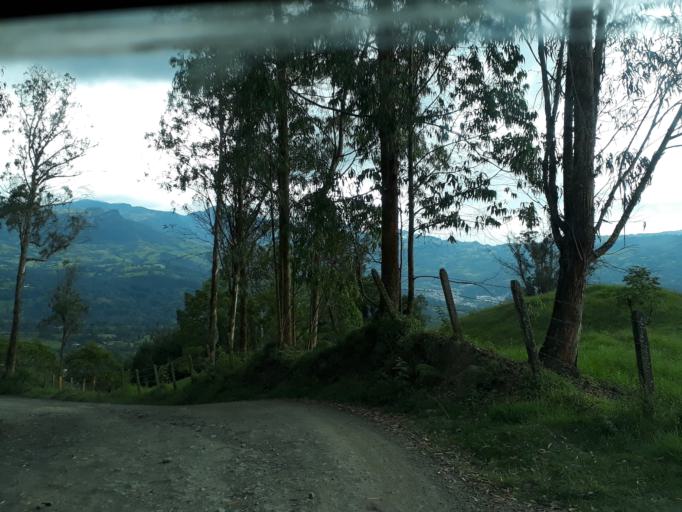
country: CO
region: Cundinamarca
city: Pacho
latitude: 5.1767
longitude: -74.1311
